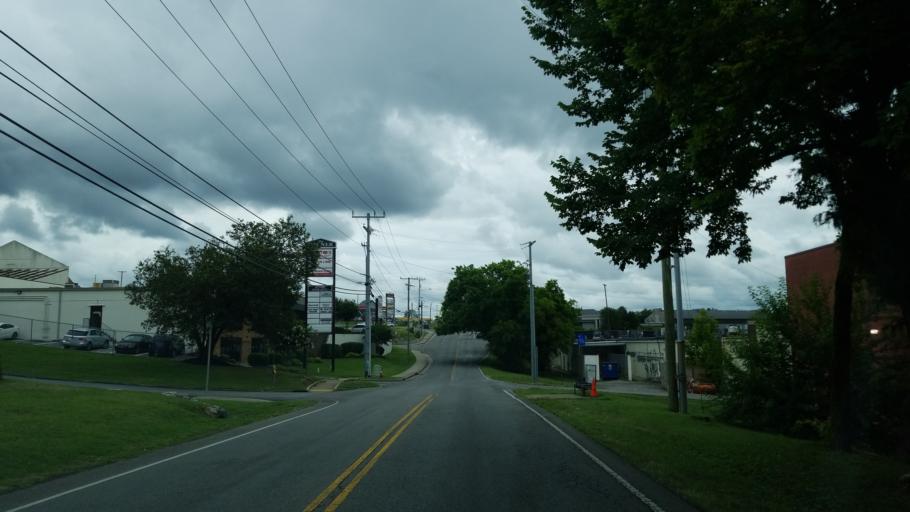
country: US
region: Tennessee
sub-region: Rutherford County
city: La Vergne
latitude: 36.0512
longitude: -86.6515
